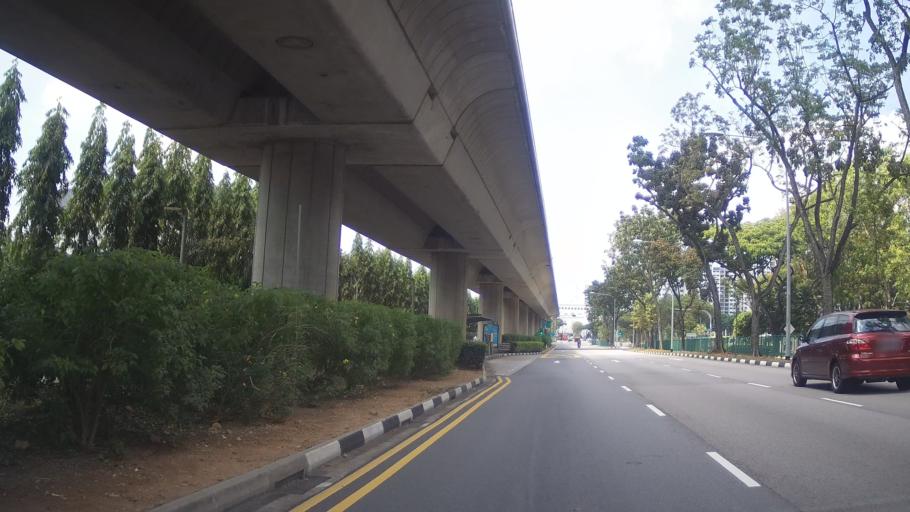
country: MY
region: Johor
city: Johor Bahru
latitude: 1.3417
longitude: 103.7128
